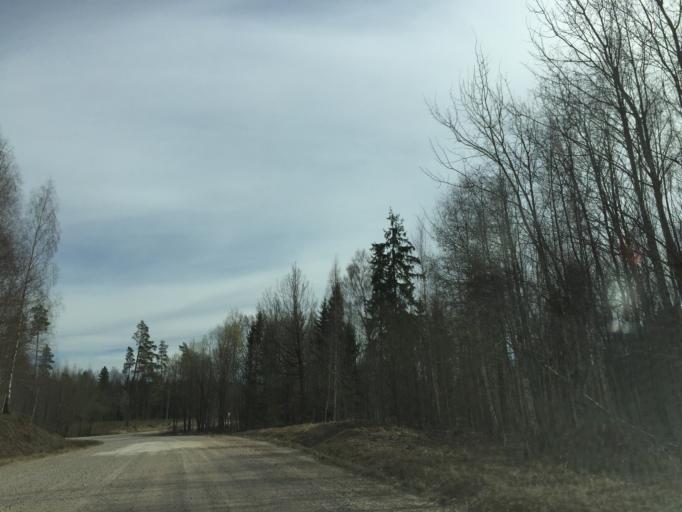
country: LV
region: Valkas Rajons
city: Valka
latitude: 57.8044
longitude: 25.9463
